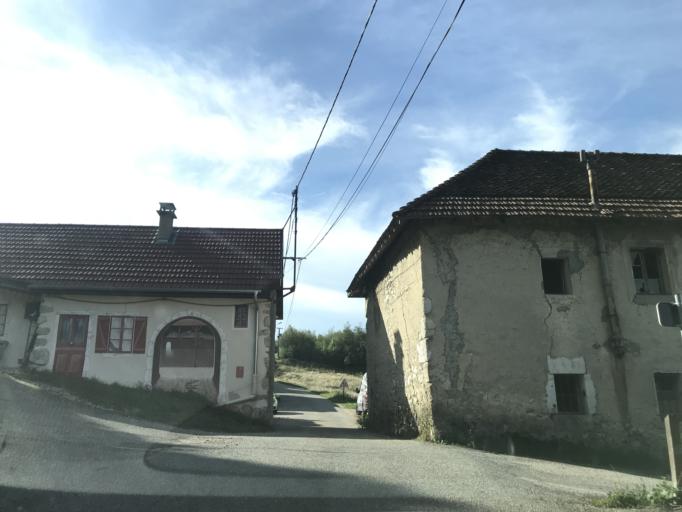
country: FR
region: Rhone-Alpes
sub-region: Departement de la Savoie
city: Novalaise
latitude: 45.6299
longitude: 5.8003
